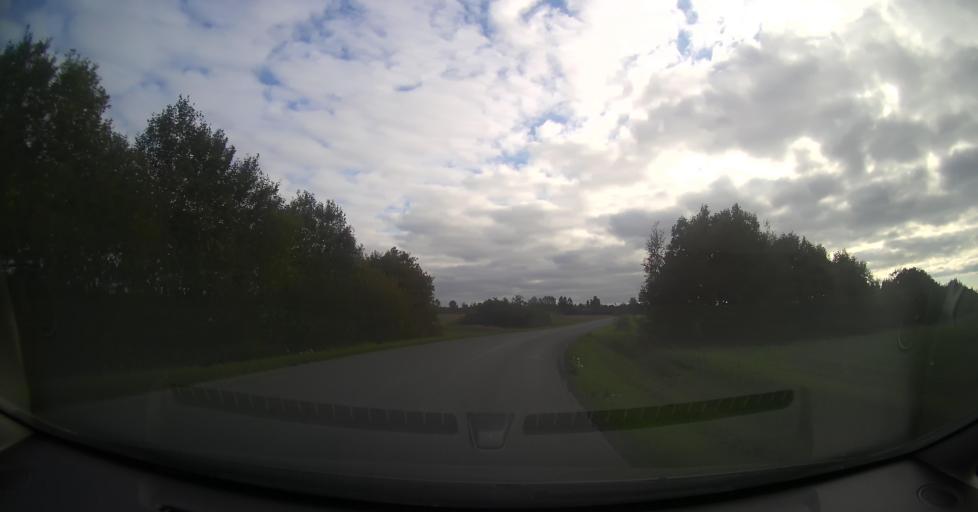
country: EE
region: Harju
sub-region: Anija vald
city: Kehra
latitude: 59.3451
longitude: 25.2526
